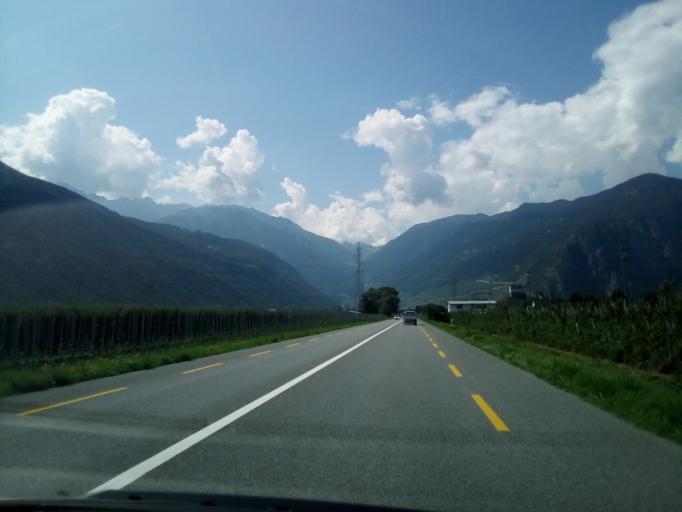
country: CH
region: Valais
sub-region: Martigny District
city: Fully
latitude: 46.1172
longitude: 7.1077
